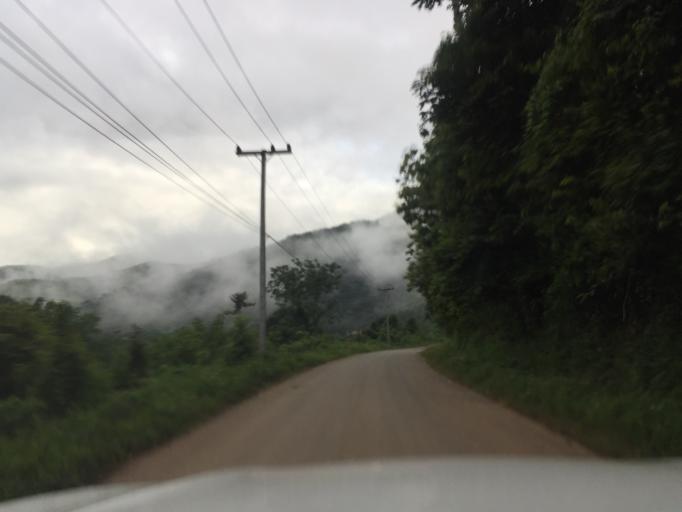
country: LA
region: Phongsali
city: Khoa
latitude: 21.0725
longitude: 102.3754
